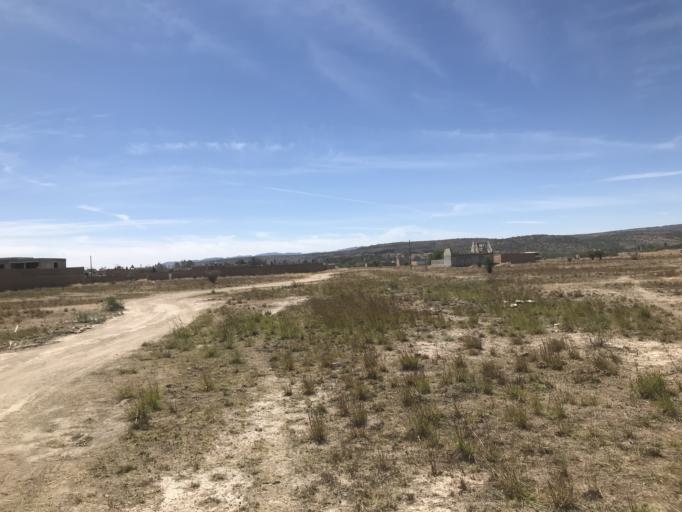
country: MX
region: Durango
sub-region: Durango
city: Sebastian Lerdo de Tejada
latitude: 23.9808
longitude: -104.6548
